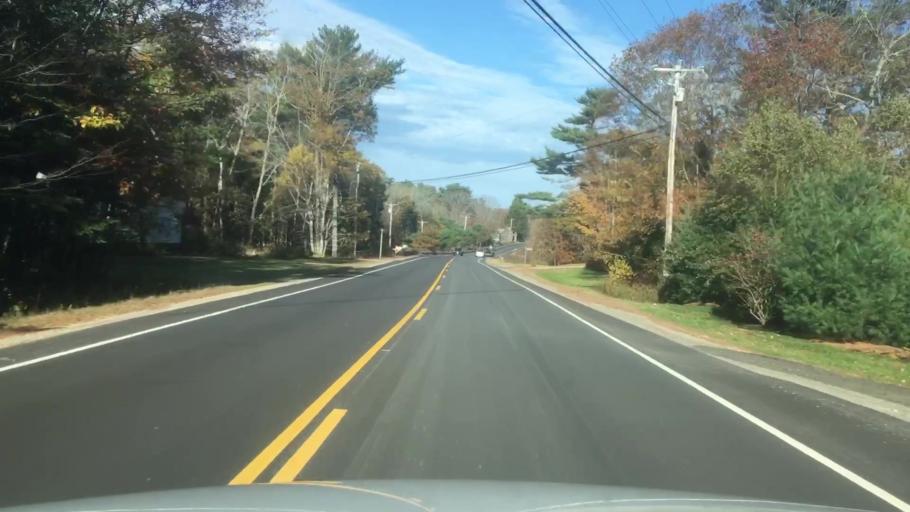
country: US
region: Maine
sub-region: Sagadahoc County
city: Woolwich
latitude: 43.8897
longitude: -69.7900
